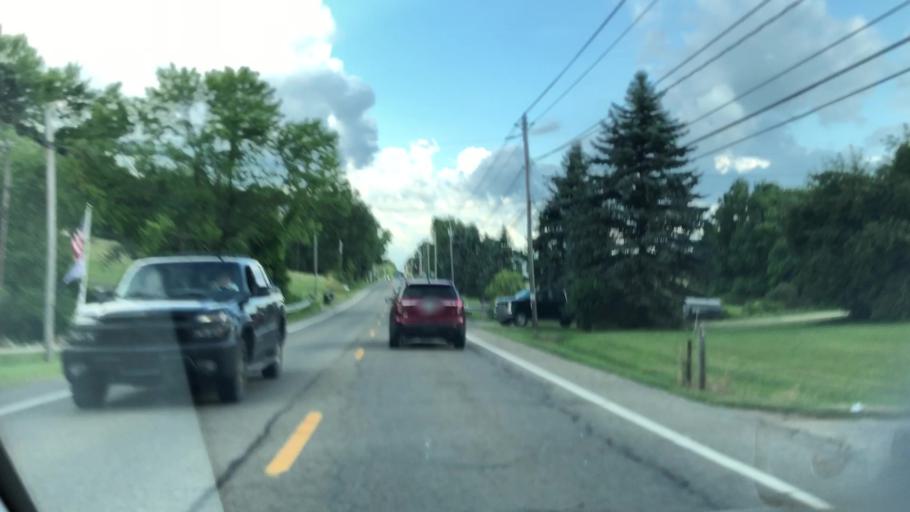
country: US
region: Ohio
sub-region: Summit County
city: Green
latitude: 40.9564
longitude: -81.4943
